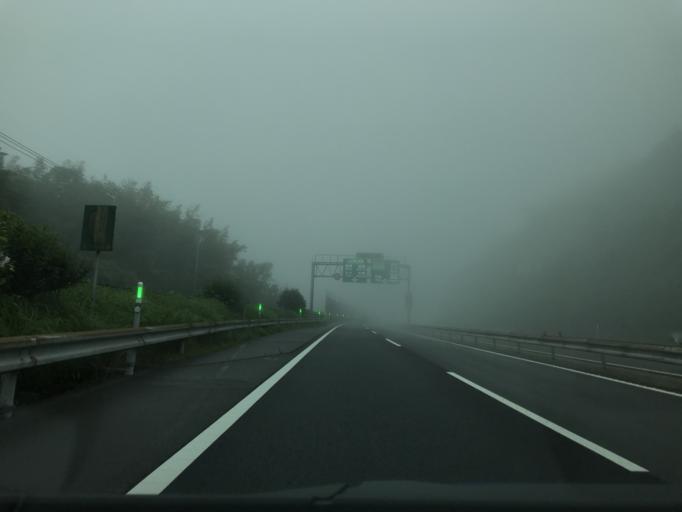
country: JP
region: Oita
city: Hiji
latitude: 33.3614
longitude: 131.4511
